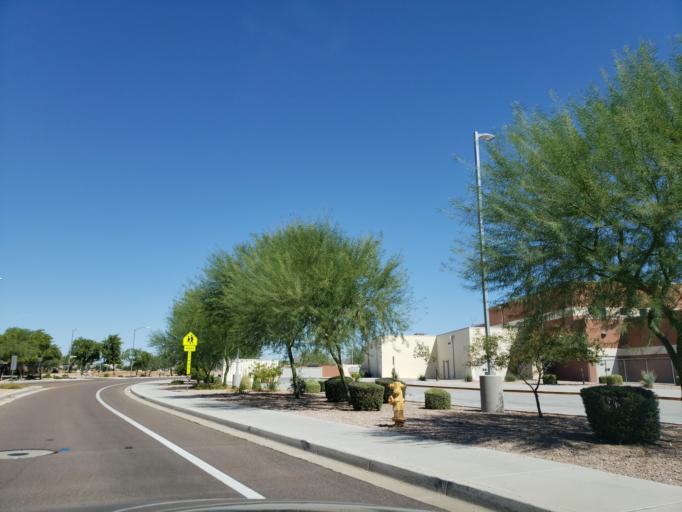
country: US
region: Arizona
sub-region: Maricopa County
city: Sun City West
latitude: 33.6785
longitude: -112.2704
